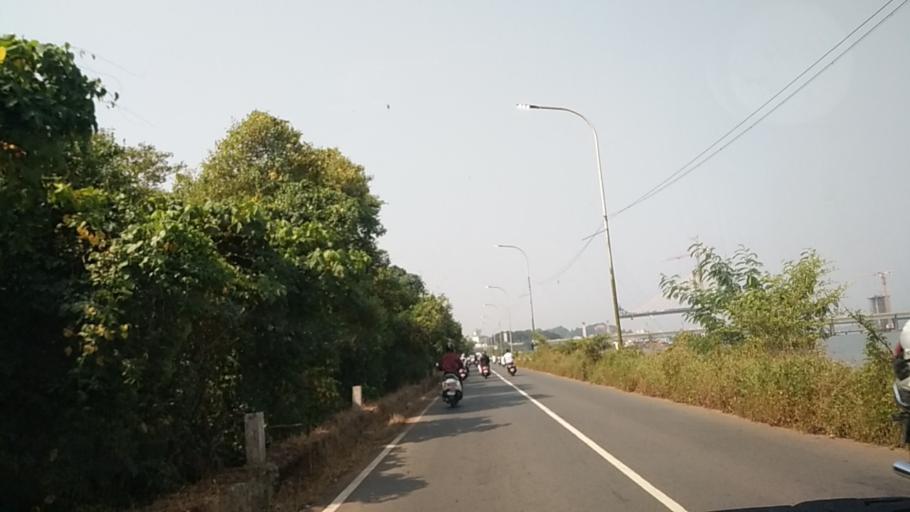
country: IN
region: Goa
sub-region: North Goa
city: Panaji
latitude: 15.5003
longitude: 73.8436
